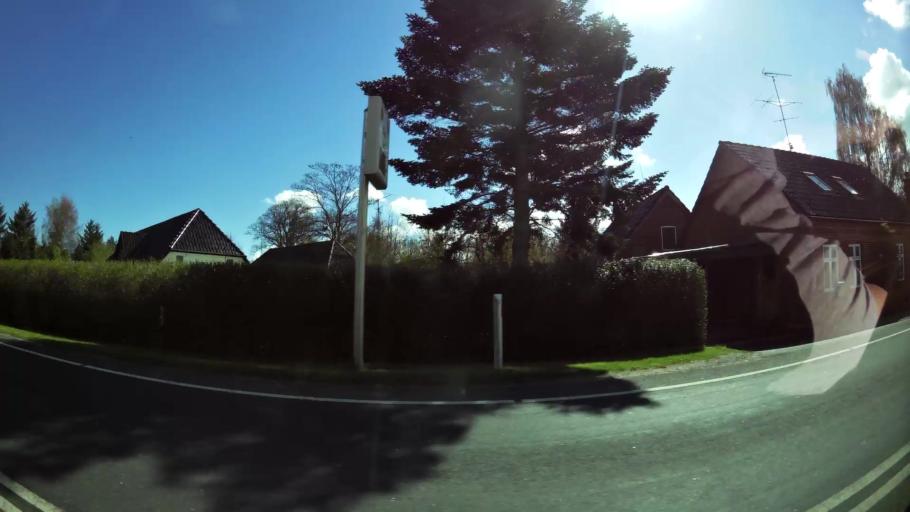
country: DK
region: South Denmark
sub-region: Middelfart Kommune
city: Brenderup
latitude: 55.4797
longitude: 9.9731
